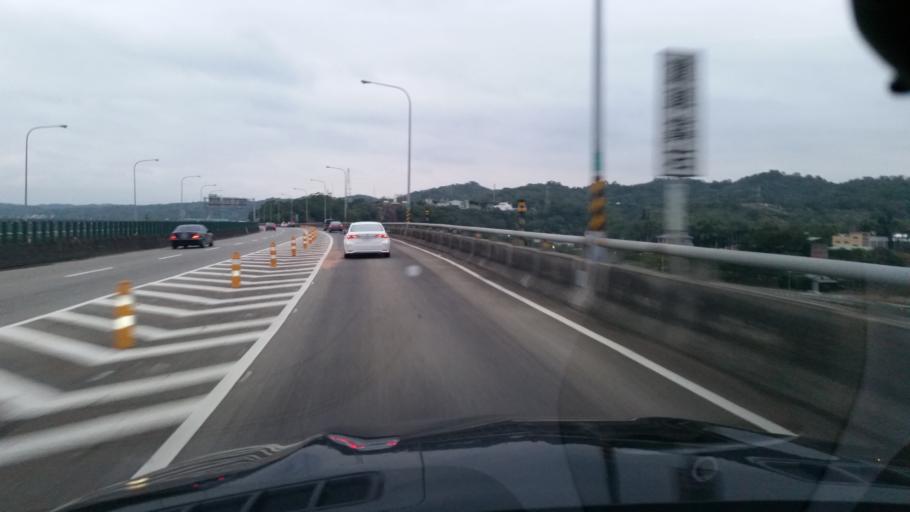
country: TW
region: Taiwan
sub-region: Miaoli
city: Miaoli
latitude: 24.5768
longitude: 120.8470
